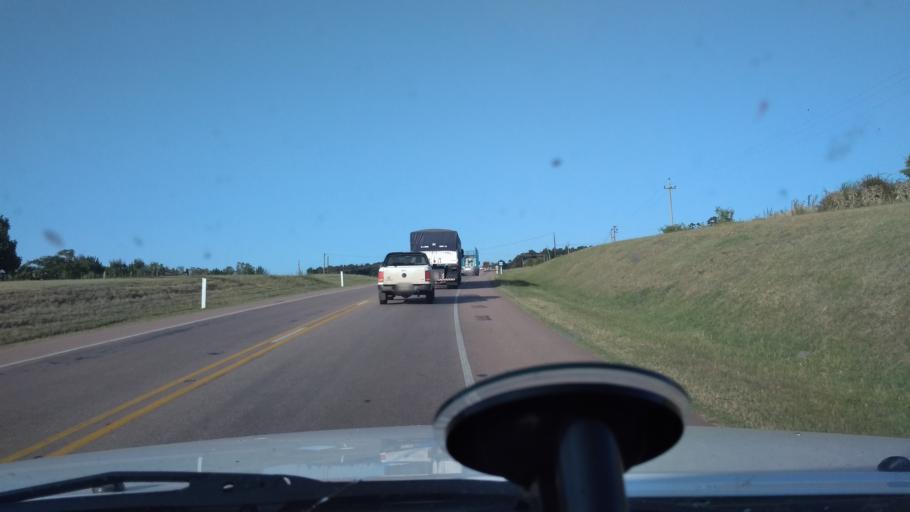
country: UY
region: Canelones
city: Canelones
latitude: -34.4682
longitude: -56.2799
